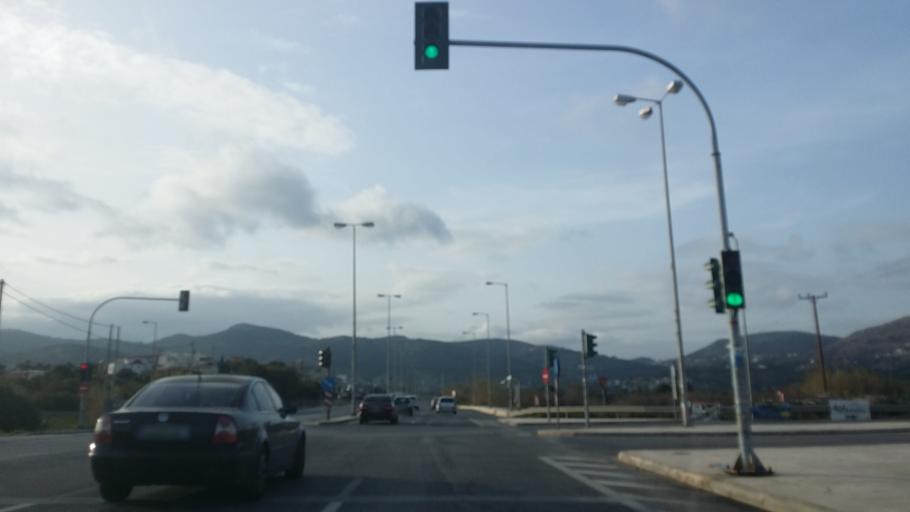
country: GR
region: Attica
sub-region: Nomarchia Anatolikis Attikis
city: Lavrio
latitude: 37.7314
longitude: 24.0521
